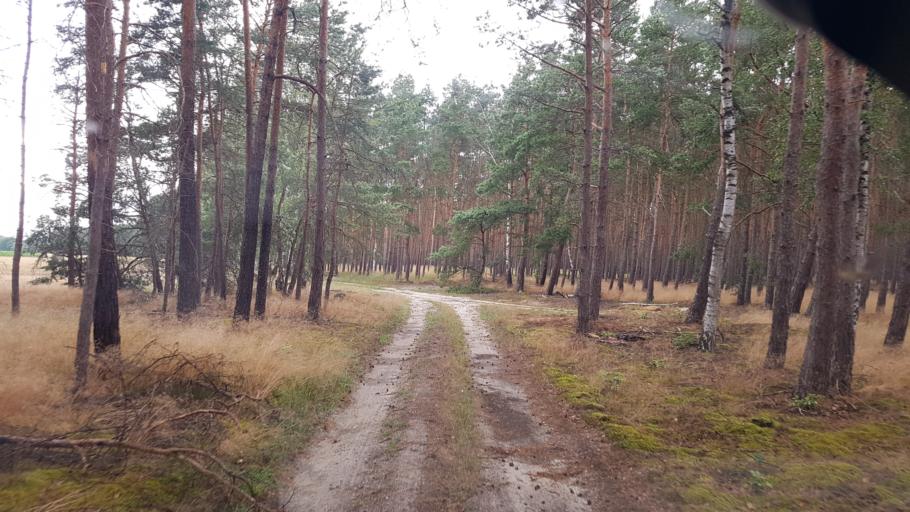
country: DE
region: Brandenburg
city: Schilda
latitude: 51.6421
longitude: 13.3435
